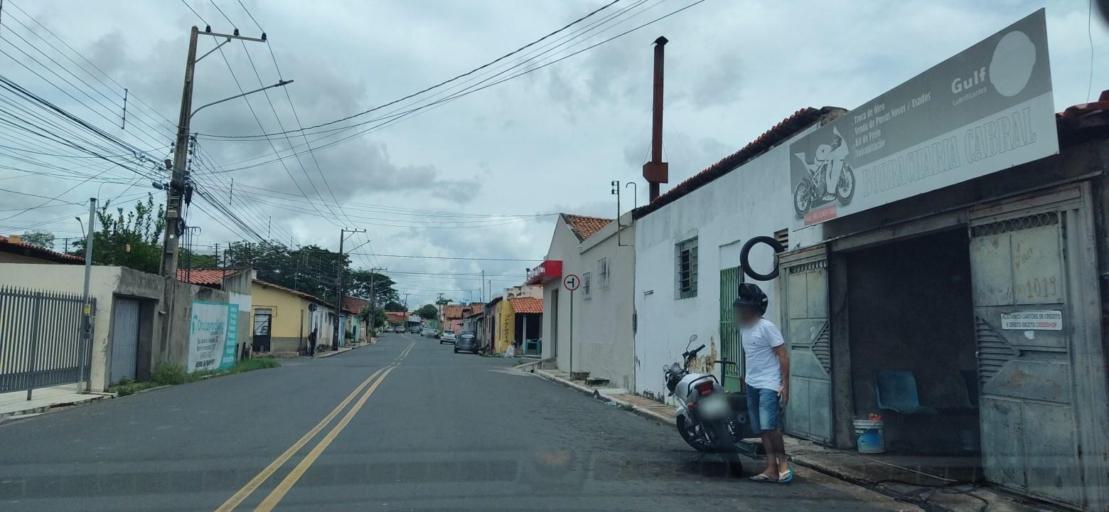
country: BR
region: Piaui
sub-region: Teresina
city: Teresina
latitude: -5.0779
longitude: -42.8057
